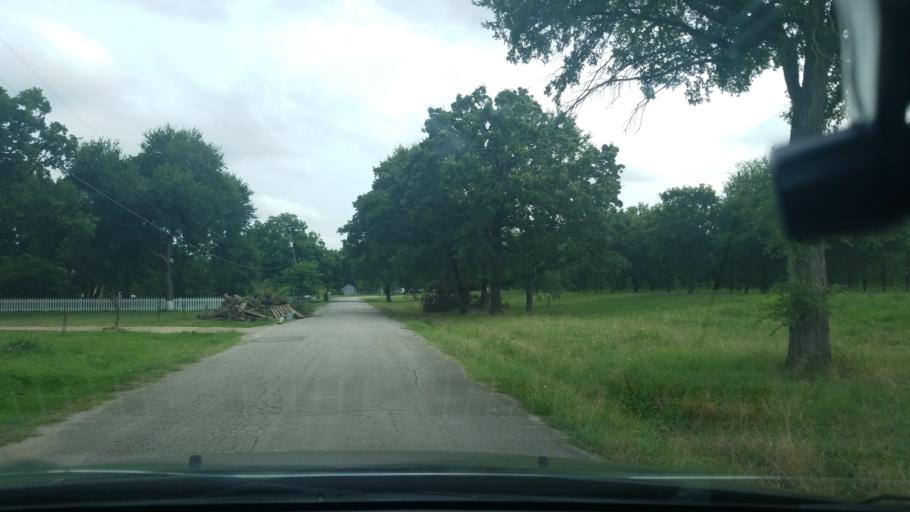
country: US
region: Texas
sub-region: Dallas County
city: Balch Springs
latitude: 32.7546
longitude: -96.6338
